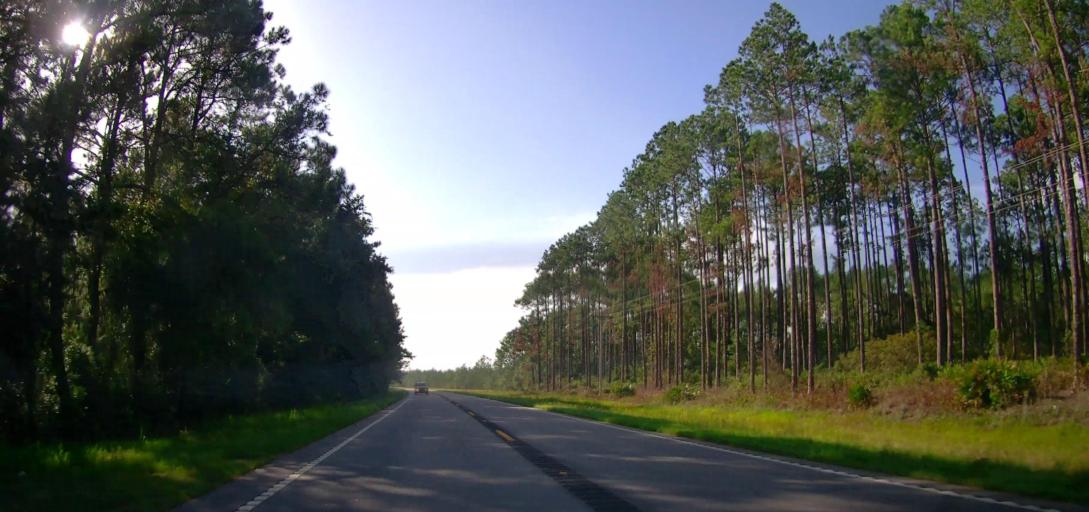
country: US
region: Georgia
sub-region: Coffee County
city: Nicholls
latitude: 31.4524
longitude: -82.7300
